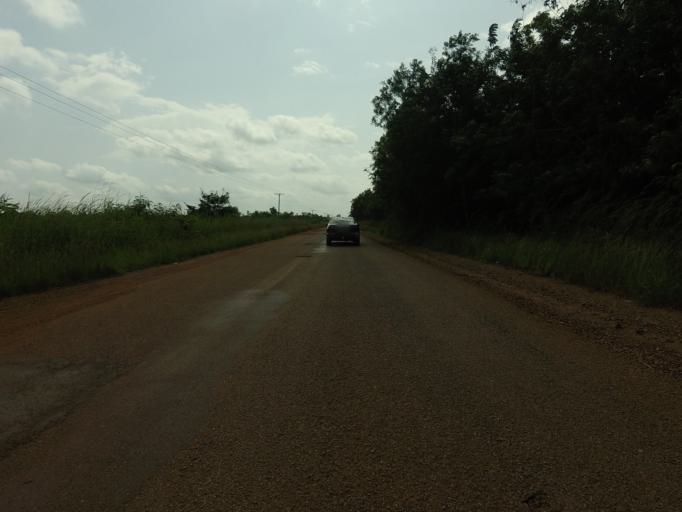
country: TG
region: Maritime
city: Lome
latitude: 6.2706
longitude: 0.9451
